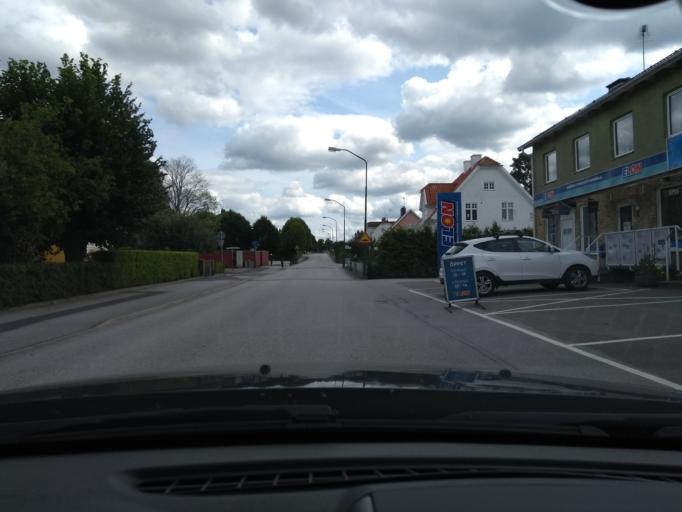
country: SE
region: Kalmar
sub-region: Vimmerby Kommun
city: Vimmerby
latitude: 57.6624
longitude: 15.8630
